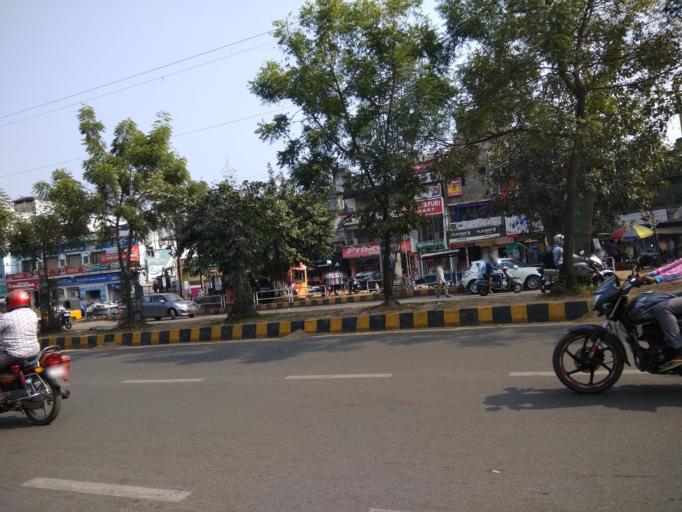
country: IN
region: Odisha
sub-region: Khordha
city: Bhubaneshwar
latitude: 20.2635
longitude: 85.8380
